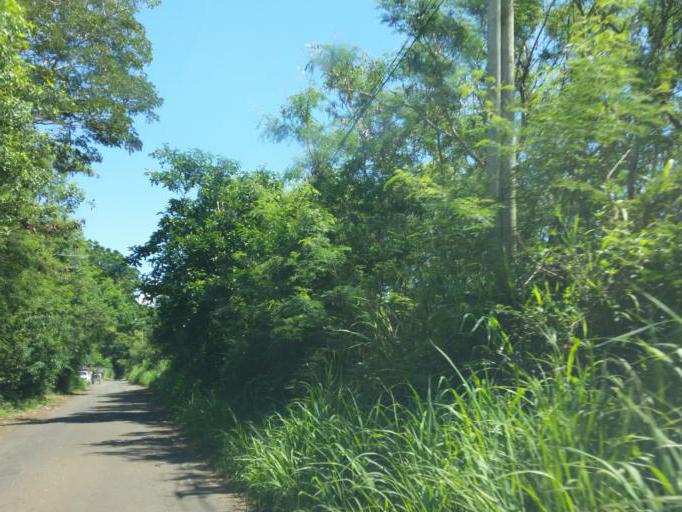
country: RE
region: Reunion
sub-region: Reunion
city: Sainte-Marie
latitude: -20.9088
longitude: 55.5168
